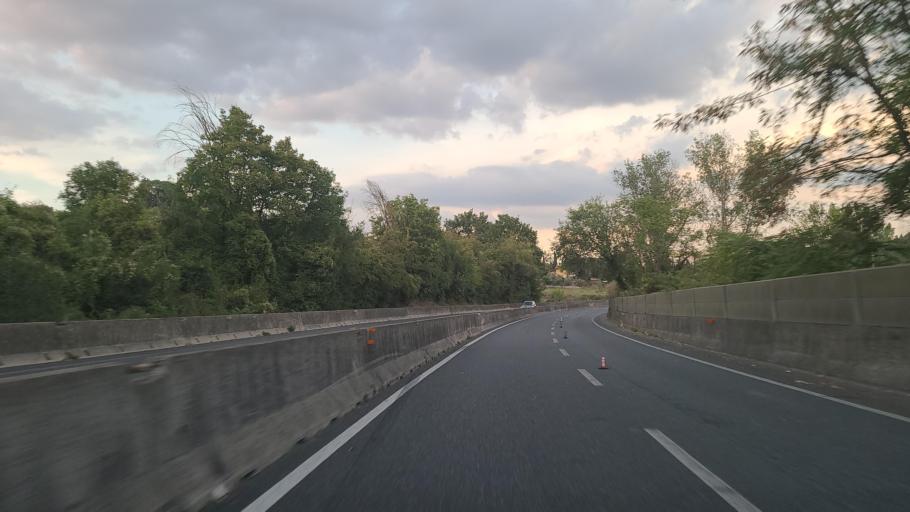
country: IT
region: Tuscany
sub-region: Province of Florence
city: Tavarnuzze
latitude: 43.7128
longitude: 11.2153
